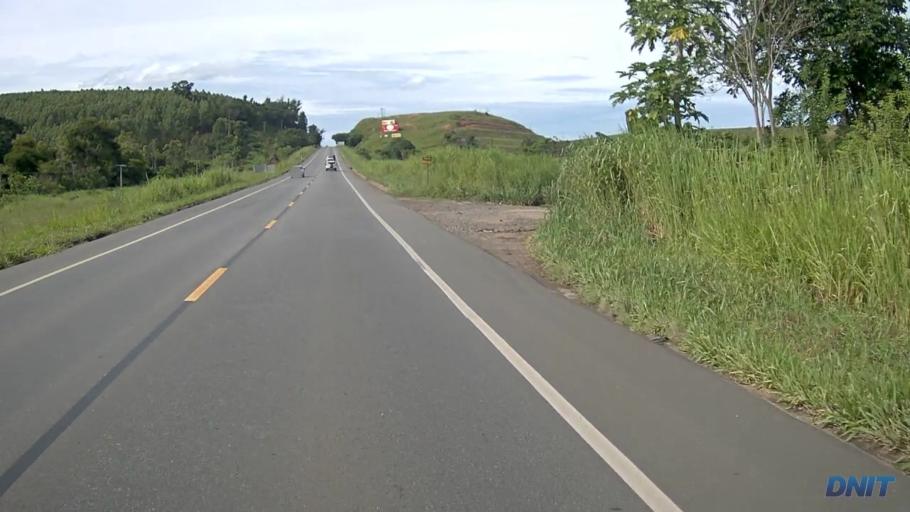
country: BR
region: Minas Gerais
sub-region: Belo Oriente
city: Belo Oriente
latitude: -19.2563
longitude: -42.3415
